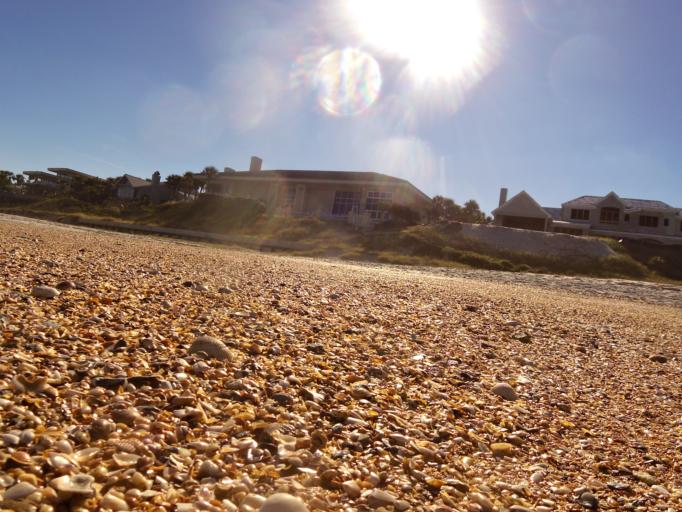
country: US
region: Florida
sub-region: Saint Johns County
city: Sawgrass
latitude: 30.1676
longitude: -81.3571
